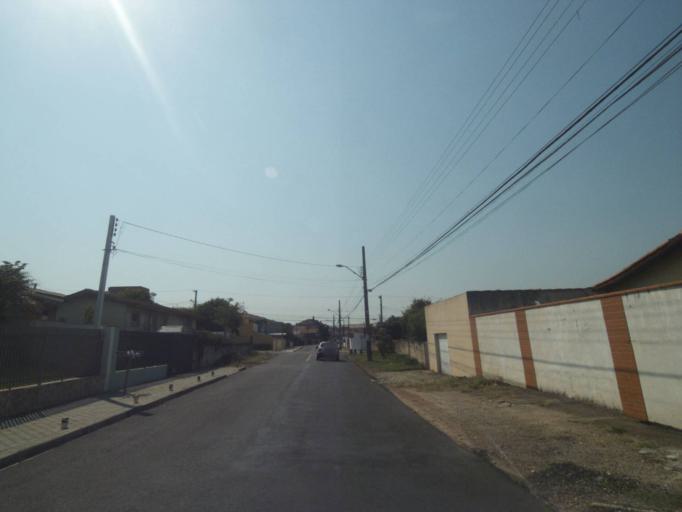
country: BR
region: Parana
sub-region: Curitiba
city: Curitiba
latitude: -25.4953
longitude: -49.2800
